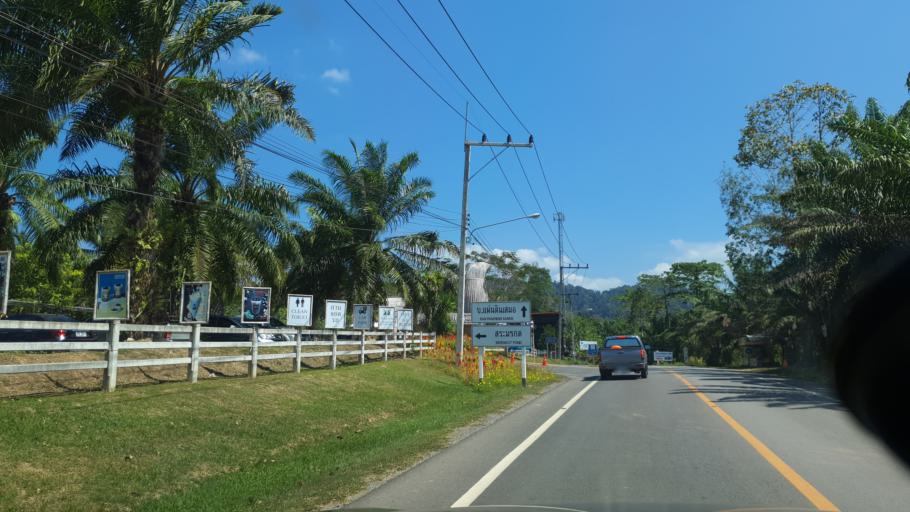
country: TH
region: Krabi
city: Khlong Thom
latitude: 7.9212
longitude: 99.2588
